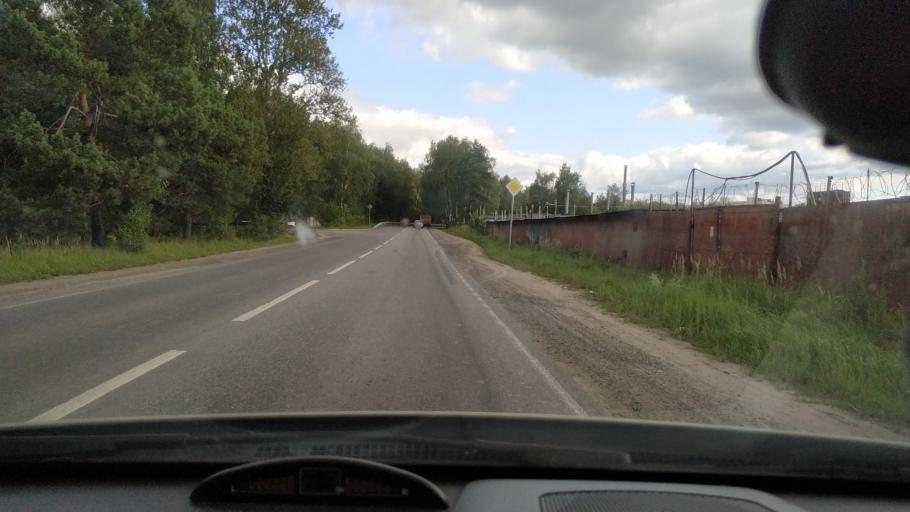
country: RU
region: Moskovskaya
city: Chornaya
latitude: 55.7653
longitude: 38.0689
